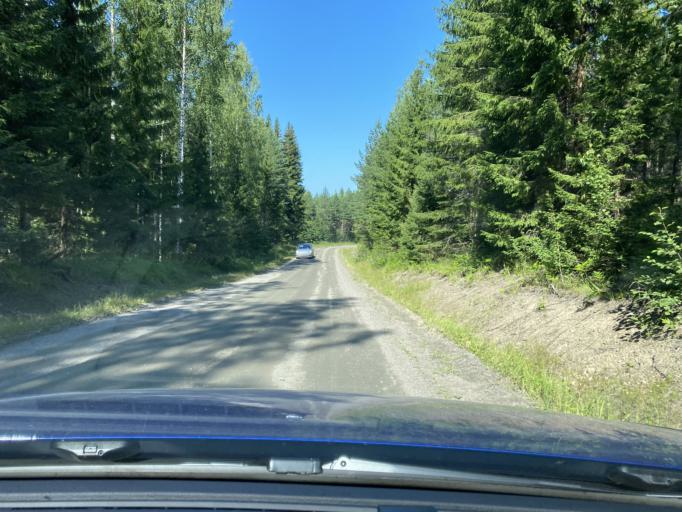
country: FI
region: Central Finland
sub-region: Jyvaeskylae
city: Korpilahti
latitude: 61.8729
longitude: 25.4154
